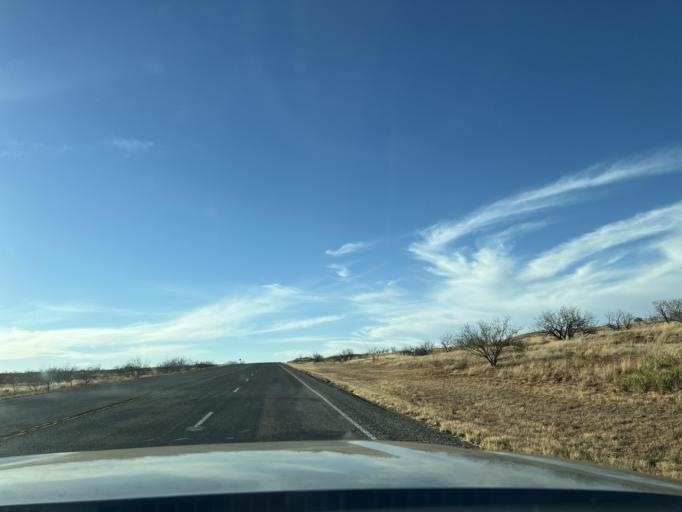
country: US
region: Texas
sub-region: Borden County
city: Gail
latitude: 32.7596
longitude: -101.2601
